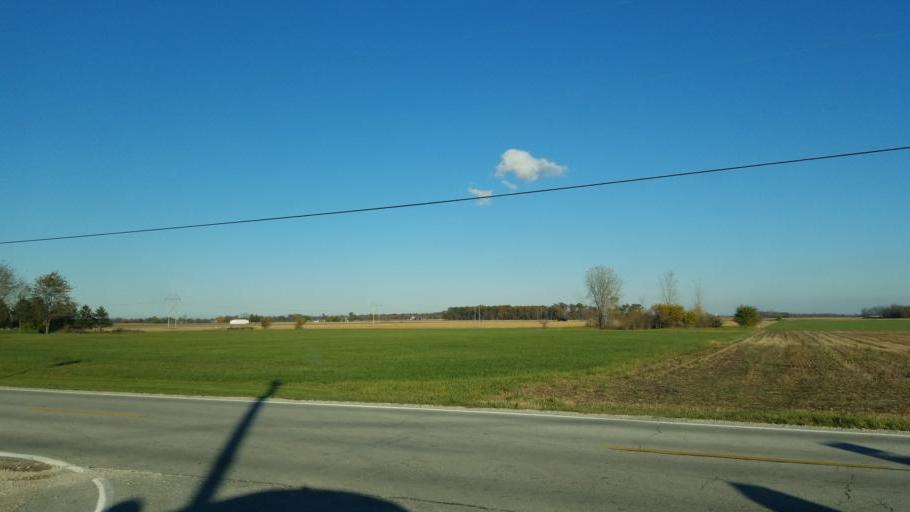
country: US
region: Ohio
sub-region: Sandusky County
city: Stony Prairie
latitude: 41.3560
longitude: -83.2237
